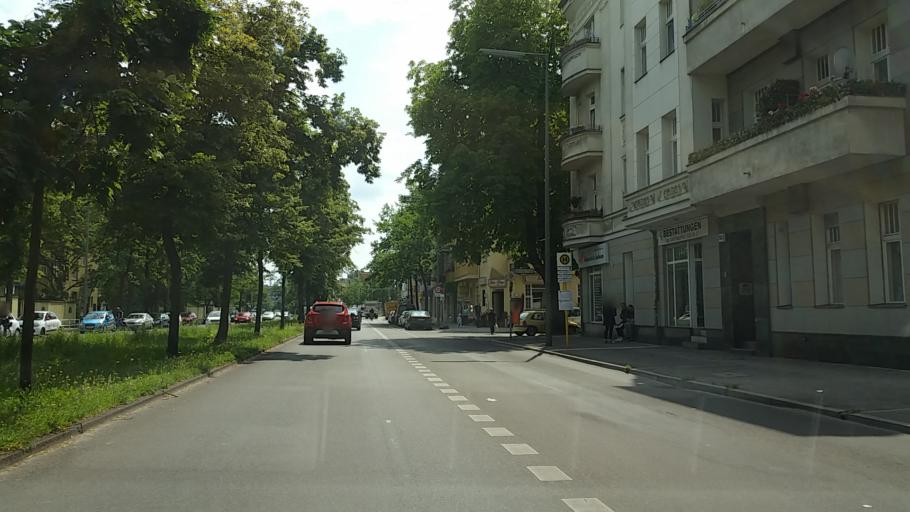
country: DE
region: Berlin
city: Hakenfelde
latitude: 52.5572
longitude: 13.2076
